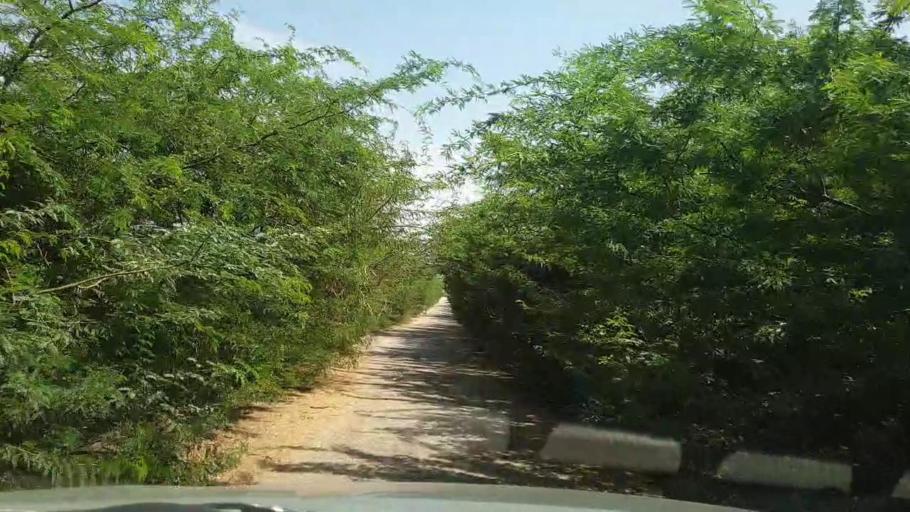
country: PK
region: Sindh
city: Bozdar
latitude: 27.0915
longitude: 68.9688
